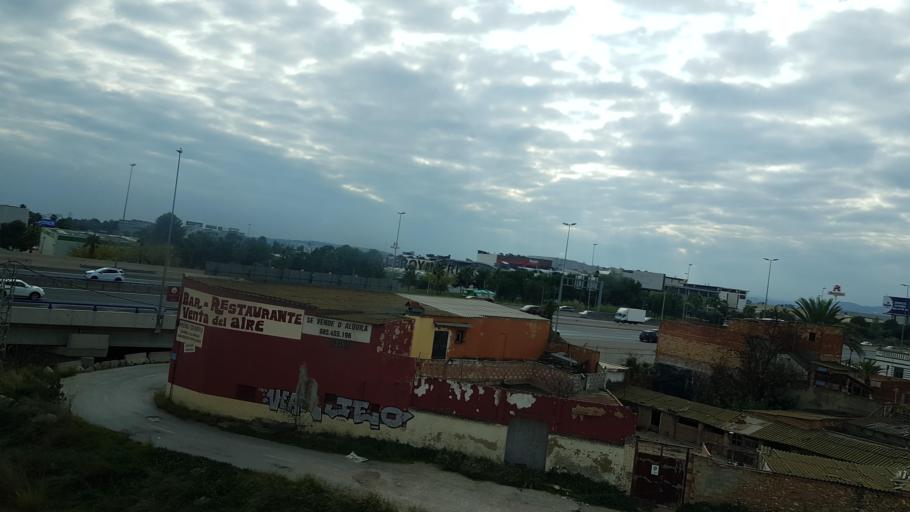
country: ES
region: Valencia
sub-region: Provincia de Valencia
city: Manises
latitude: 39.4756
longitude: -0.4863
